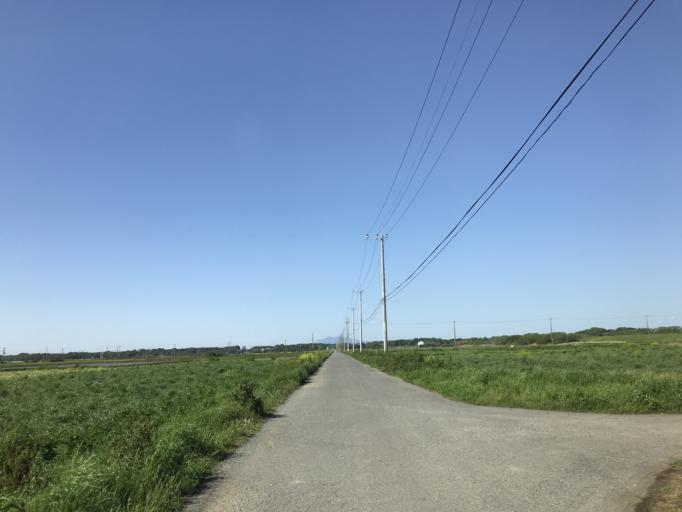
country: JP
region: Ibaraki
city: Moriya
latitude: 35.9512
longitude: 139.9369
